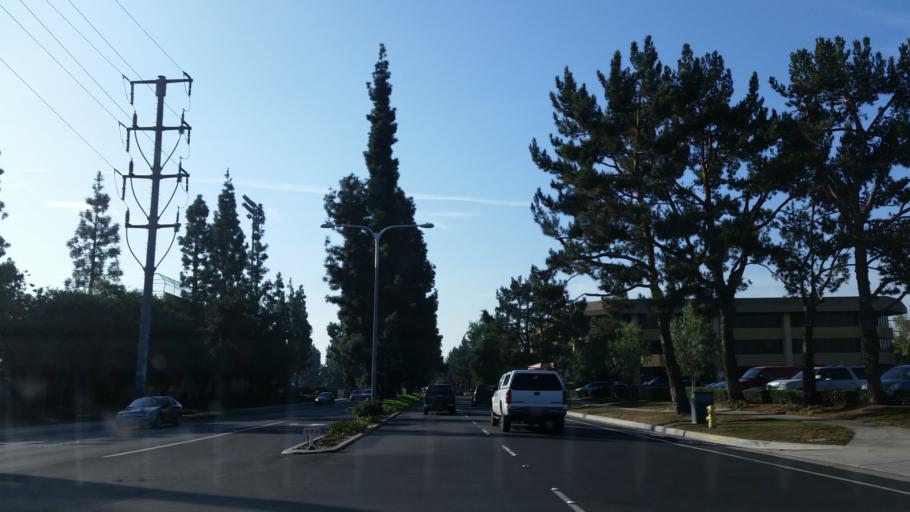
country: US
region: California
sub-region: Los Angeles County
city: Bellflower
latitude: 33.8759
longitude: -118.0998
